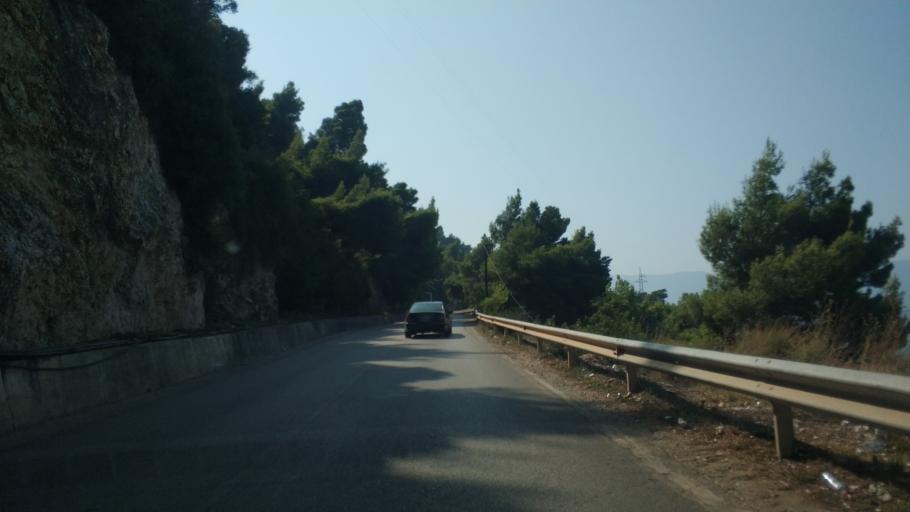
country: AL
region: Vlore
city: Vlore
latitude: 40.4082
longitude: 19.4807
